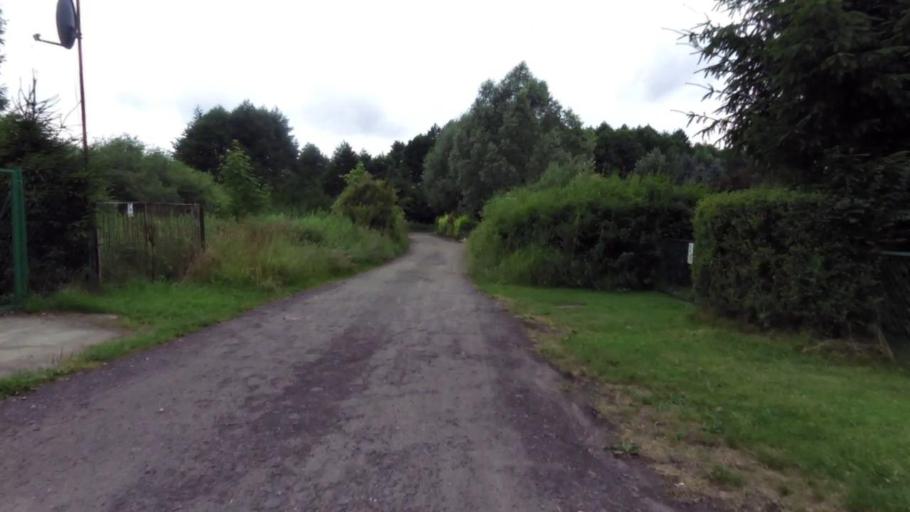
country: PL
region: West Pomeranian Voivodeship
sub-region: Powiat mysliborski
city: Mysliborz
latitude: 52.9531
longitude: 14.8710
